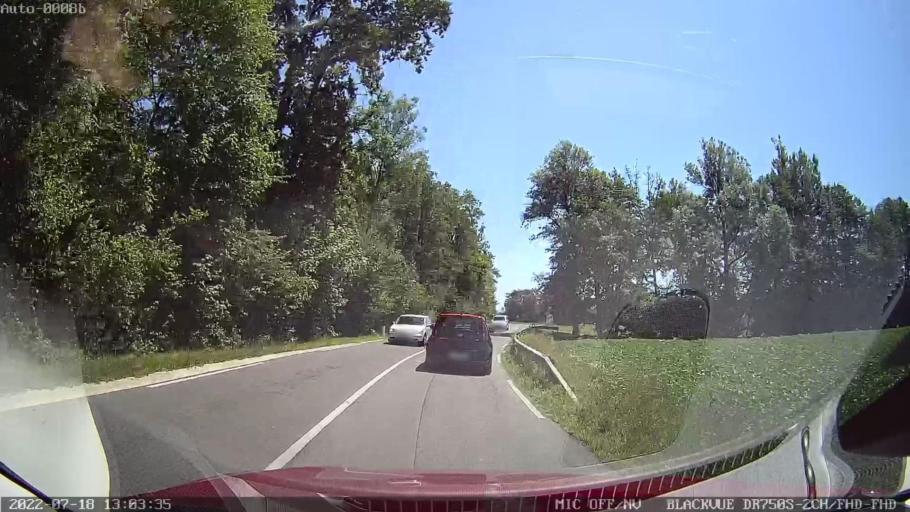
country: SI
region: Brezovica
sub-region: Opstina Ljubljana-Vic-Rudnik
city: Brezovica pri Ljubljani
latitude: 46.0496
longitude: 14.4345
